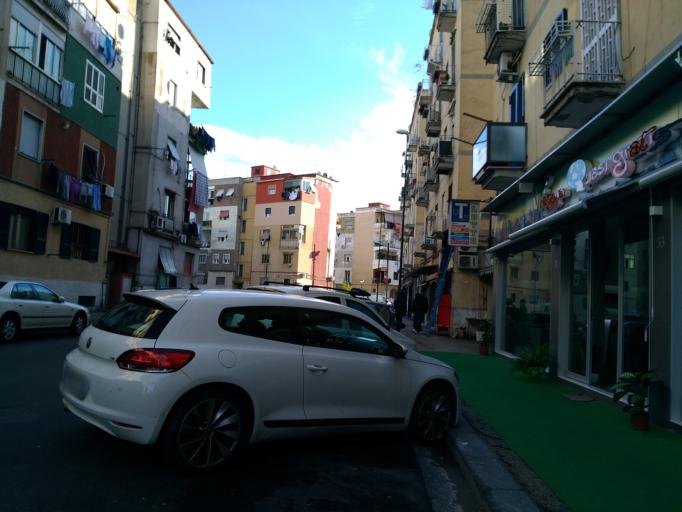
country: IT
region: Campania
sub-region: Provincia di Napoli
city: Arpino
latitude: 40.8588
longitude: 14.2929
